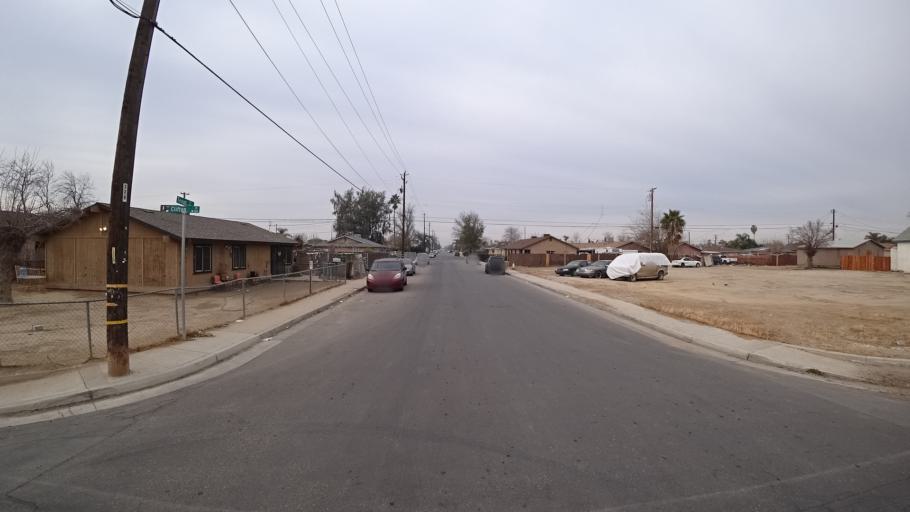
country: US
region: California
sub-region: Kern County
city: Bakersfield
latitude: 35.3576
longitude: -118.9864
